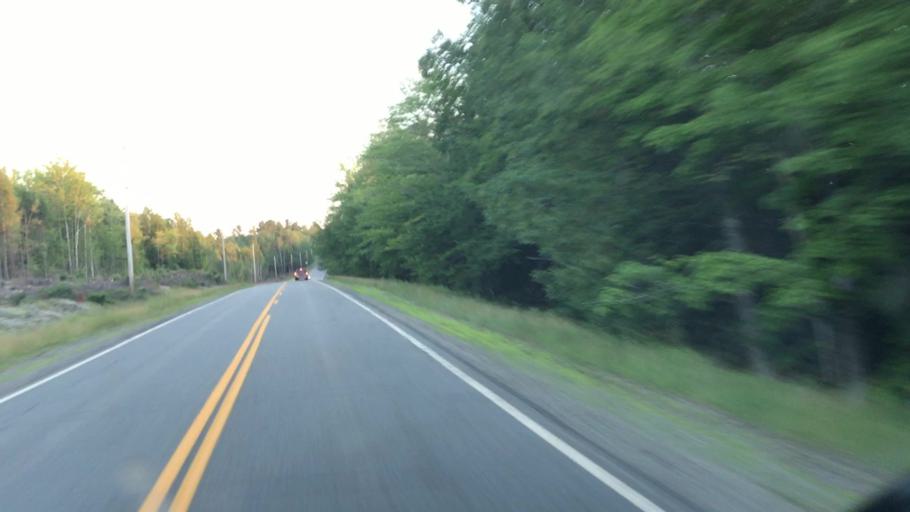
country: US
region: Maine
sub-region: Penobscot County
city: Medway
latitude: 45.5923
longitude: -68.3125
